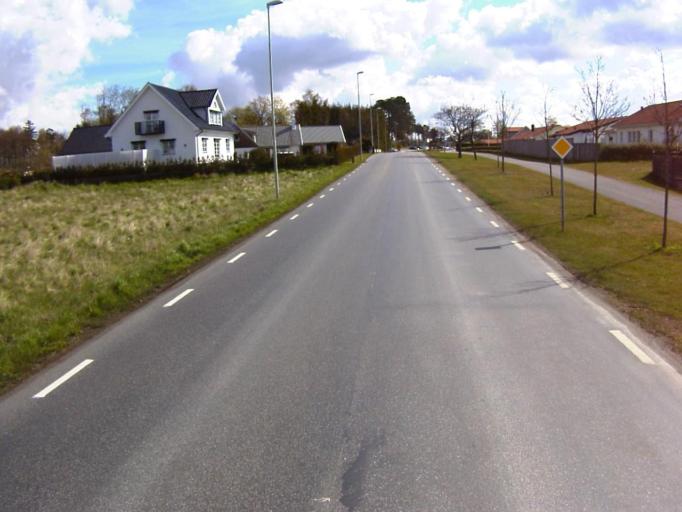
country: SE
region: Skane
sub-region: Kristianstads Kommun
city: Kristianstad
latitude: 56.0103
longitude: 14.0927
